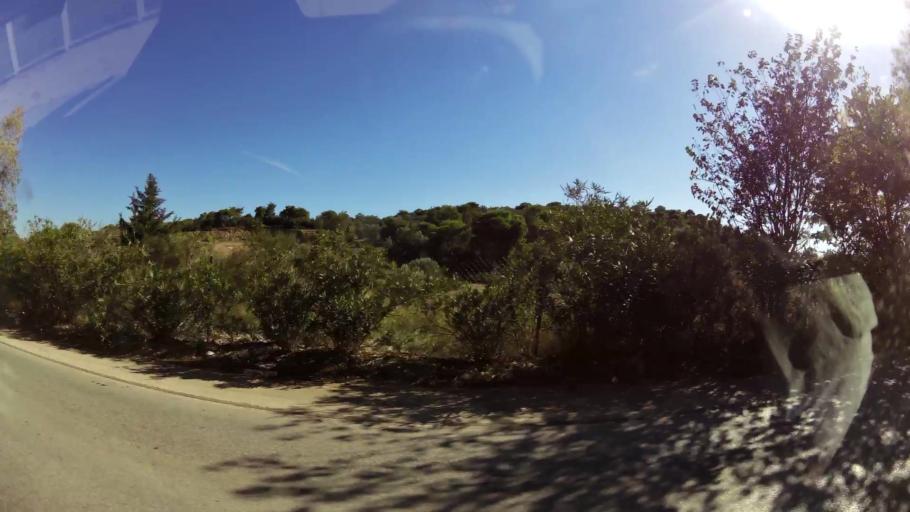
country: GR
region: Attica
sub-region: Nomarchia Anatolikis Attikis
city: Leondarion
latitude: 37.9786
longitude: 23.8663
